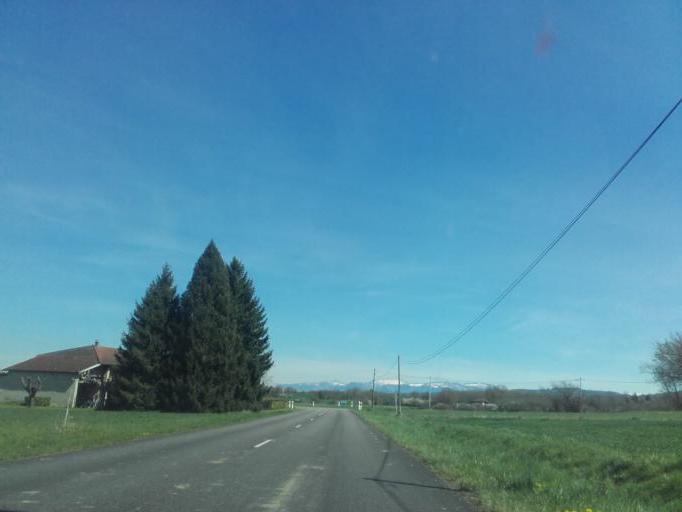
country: FR
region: Rhone-Alpes
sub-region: Departement de l'Isere
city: Saint-Simeon-de-Bressieux
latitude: 45.3305
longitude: 5.2868
